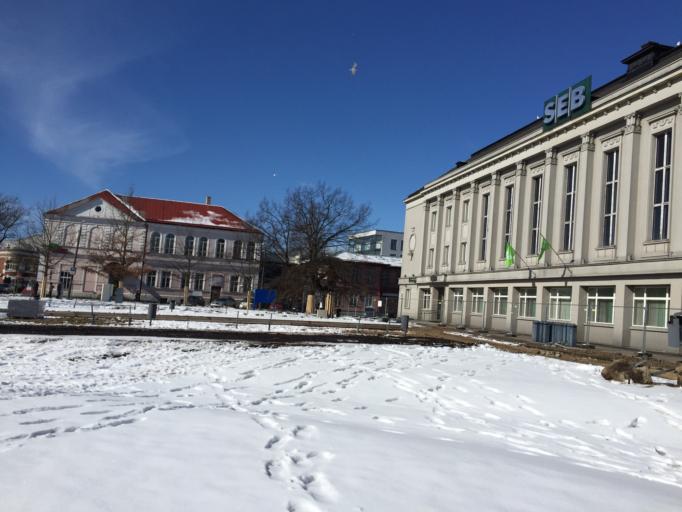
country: EE
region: Paernumaa
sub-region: Paernu linn
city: Parnu
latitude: 58.3852
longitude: 24.5057
